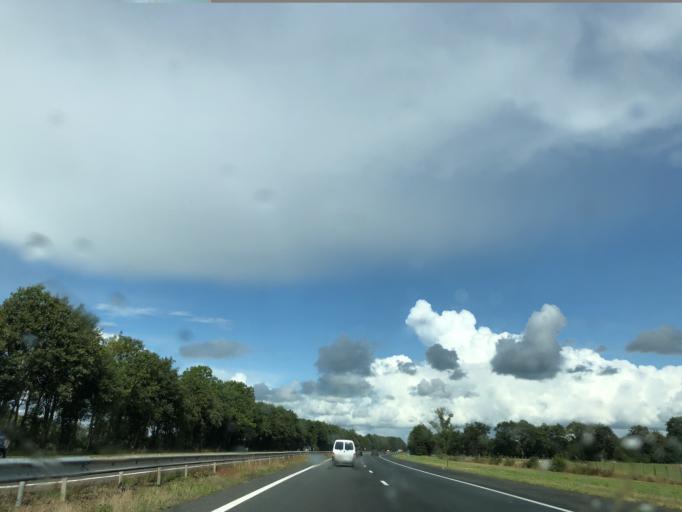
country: NL
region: Friesland
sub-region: Gemeente Smallingerland
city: Drachtstercompagnie
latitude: 53.1199
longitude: 6.1618
